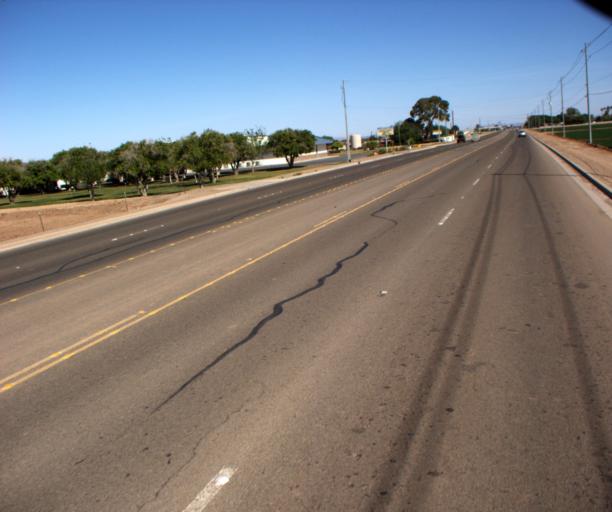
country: US
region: Arizona
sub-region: Yuma County
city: Yuma
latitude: 32.6563
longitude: -114.6500
